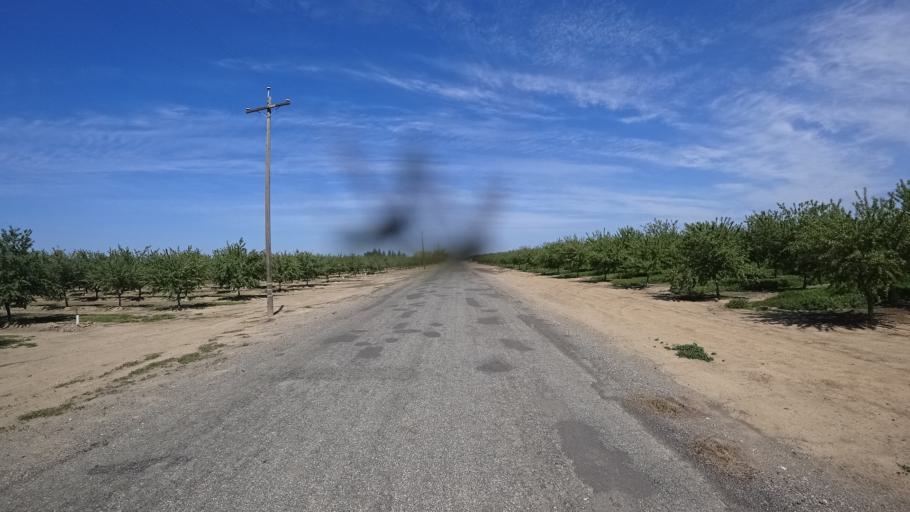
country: US
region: California
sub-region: Glenn County
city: Hamilton City
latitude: 39.6463
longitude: -122.0743
